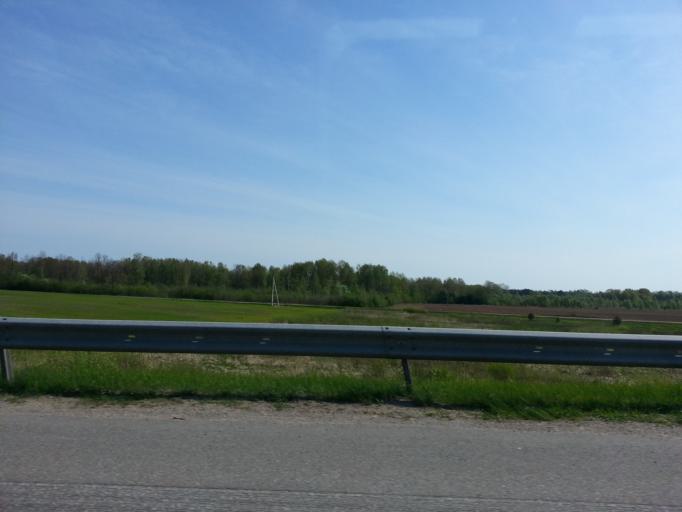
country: LT
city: Sirvintos
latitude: 54.8919
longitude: 25.0540
